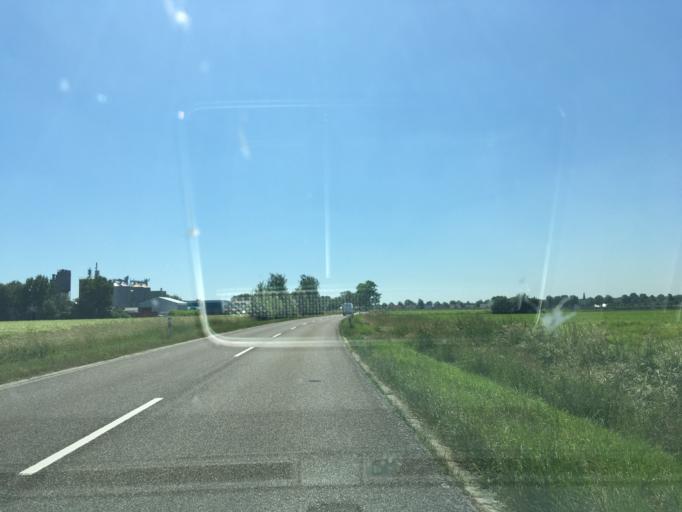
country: DE
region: North Rhine-Westphalia
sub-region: Regierungsbezirk Munster
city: Raesfeld
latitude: 51.7786
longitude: 6.8273
